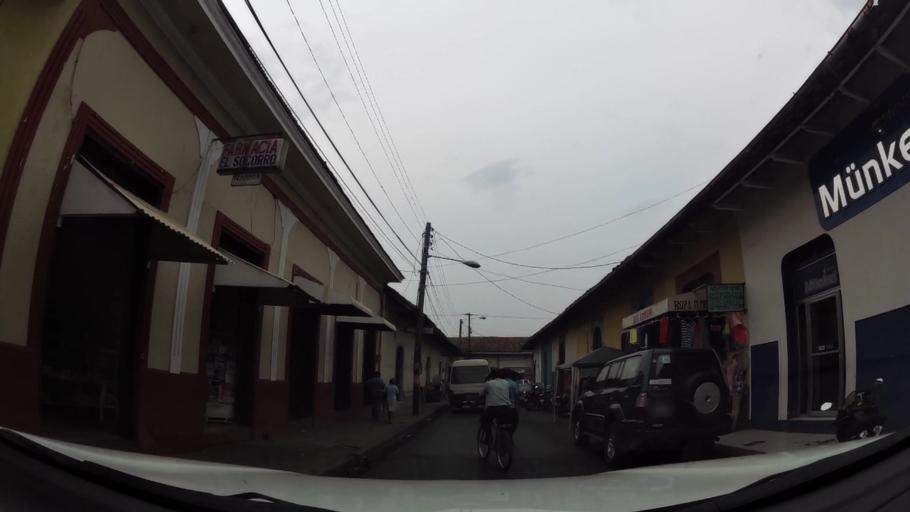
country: NI
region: Leon
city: Leon
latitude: 12.4381
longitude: -86.8758
